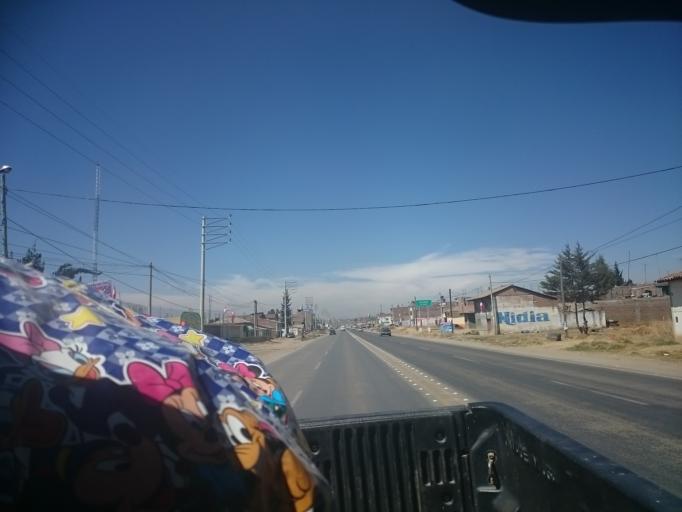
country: PE
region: Junin
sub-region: Provincia de Huancayo
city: San Agustin
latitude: -11.9918
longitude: -75.2571
